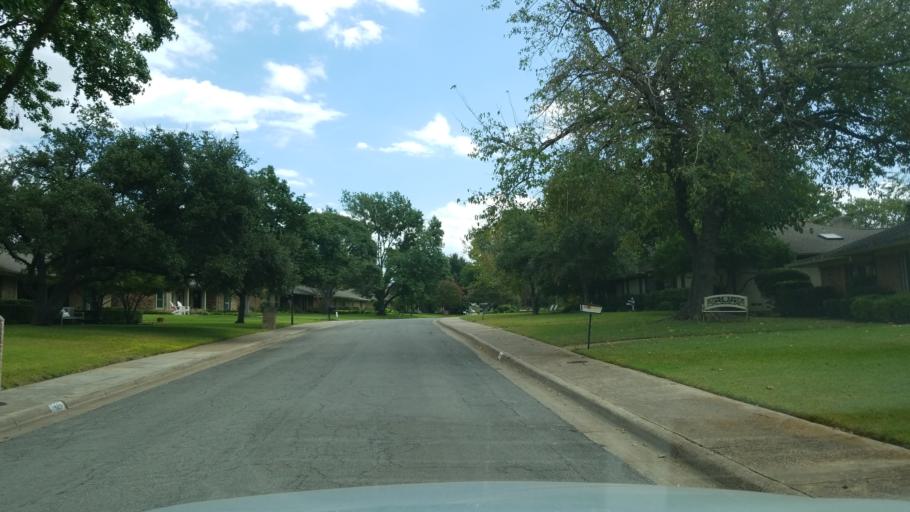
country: US
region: Texas
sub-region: Dallas County
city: Addison
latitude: 32.9529
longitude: -96.7809
